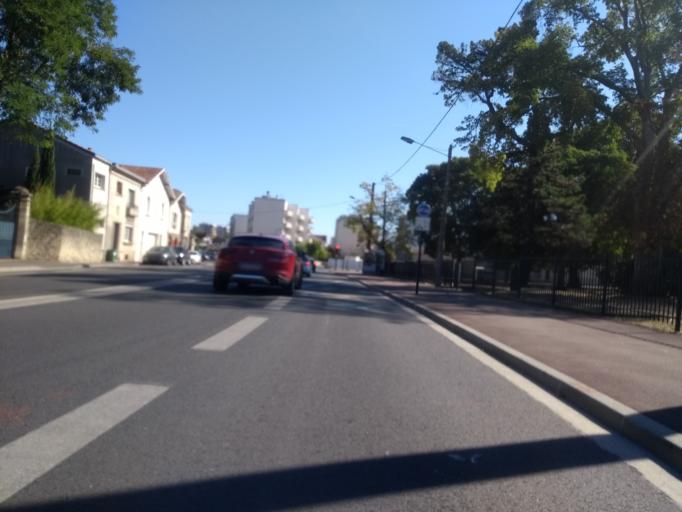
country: FR
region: Aquitaine
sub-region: Departement de la Gironde
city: Le Bouscat
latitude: 44.8555
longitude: -0.6149
